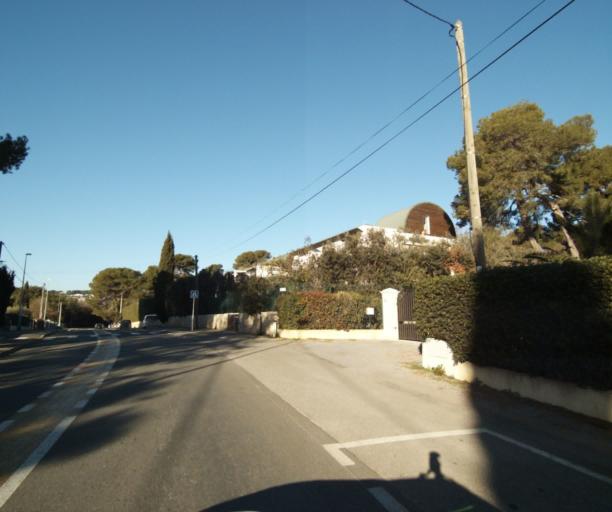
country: FR
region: Provence-Alpes-Cote d'Azur
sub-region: Departement des Alpes-Maritimes
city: Vallauris
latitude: 43.5961
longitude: 7.0798
